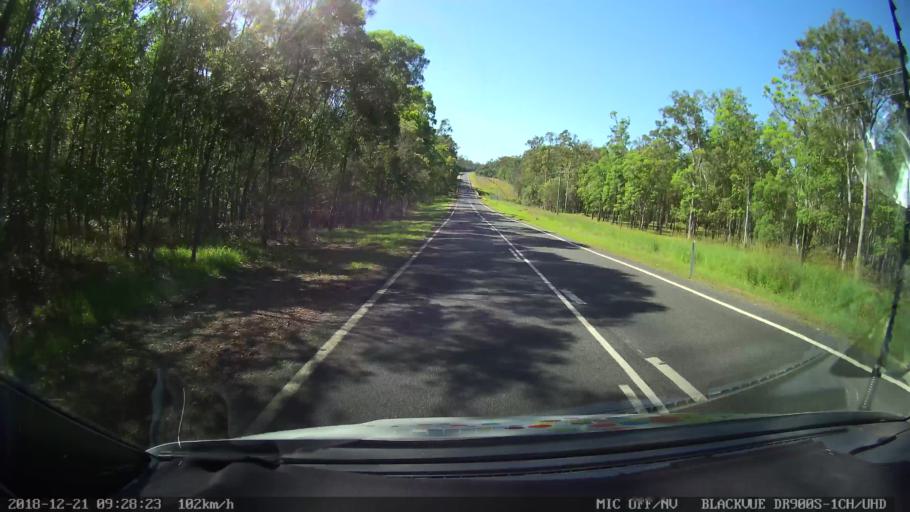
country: AU
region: New South Wales
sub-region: Clarence Valley
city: Maclean
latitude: -29.4167
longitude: 152.9865
